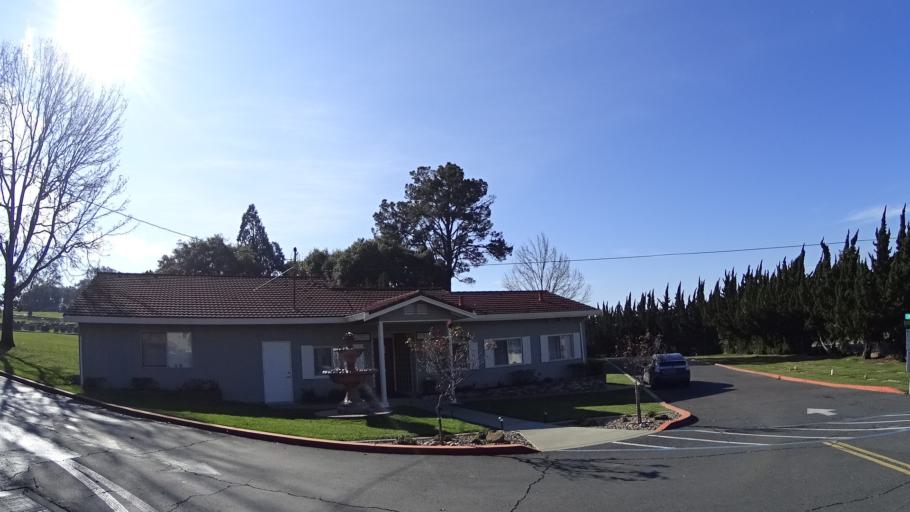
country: US
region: California
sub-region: Alameda County
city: Fairview
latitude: 37.6768
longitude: -122.0491
